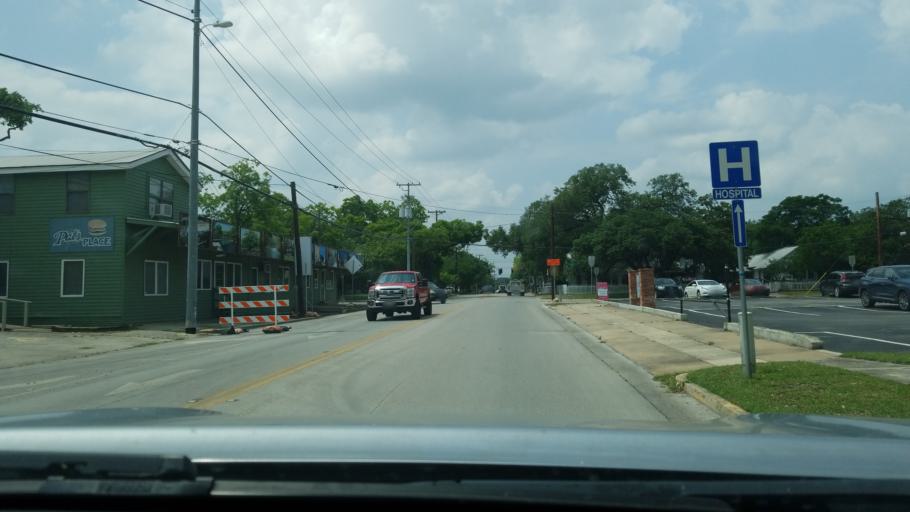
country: US
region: Texas
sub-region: Comal County
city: New Braunfels
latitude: 29.7085
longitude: -98.1188
